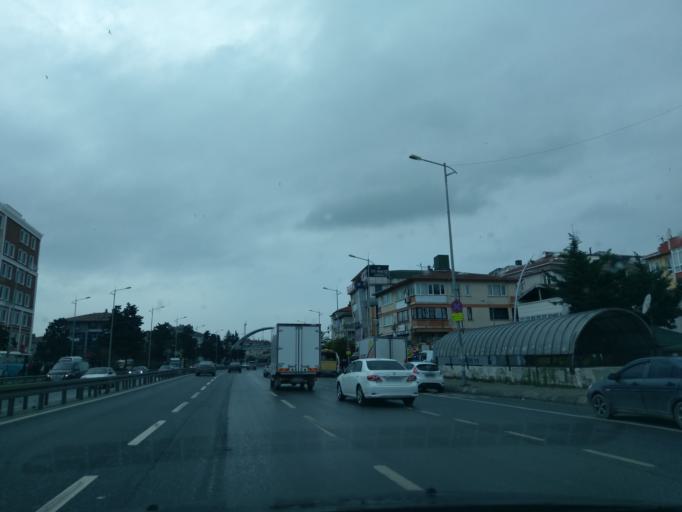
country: TR
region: Istanbul
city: Bueyuekcekmece
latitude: 41.0218
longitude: 28.5834
